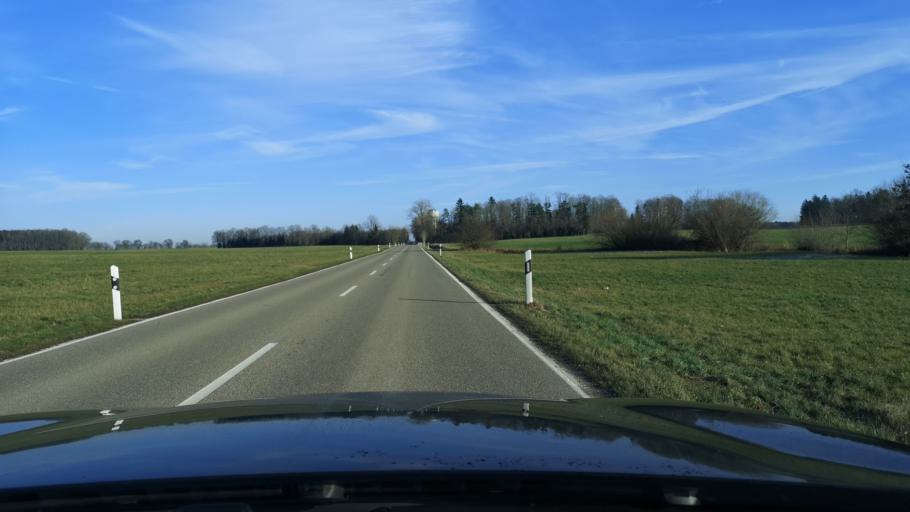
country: DE
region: Baden-Wuerttemberg
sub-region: Regierungsbezirk Stuttgart
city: Eschach
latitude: 48.8881
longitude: 9.8836
